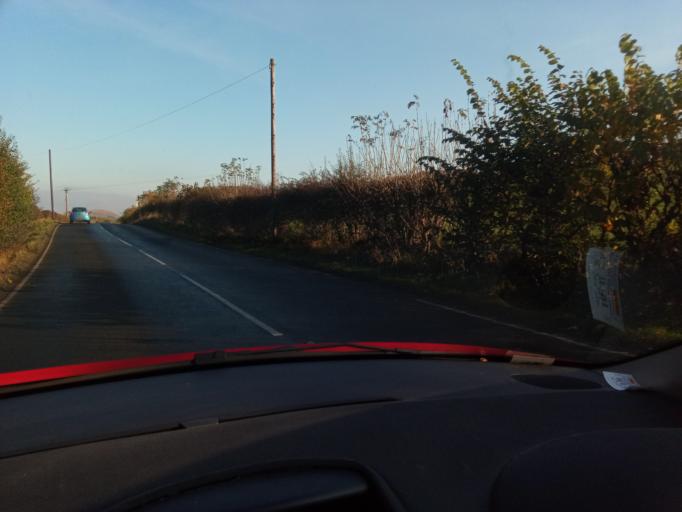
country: GB
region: Scotland
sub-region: The Scottish Borders
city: Hawick
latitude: 55.4383
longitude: -2.7481
